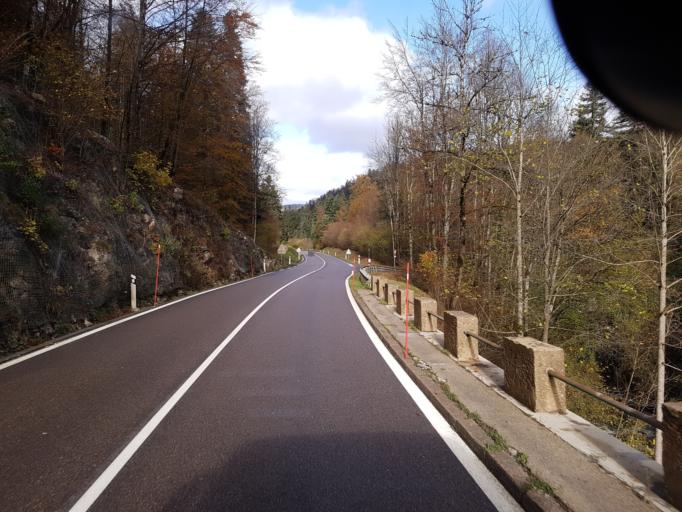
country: FR
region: Franche-Comte
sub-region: Departement du Jura
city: Champagnole
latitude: 46.6697
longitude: 5.9389
